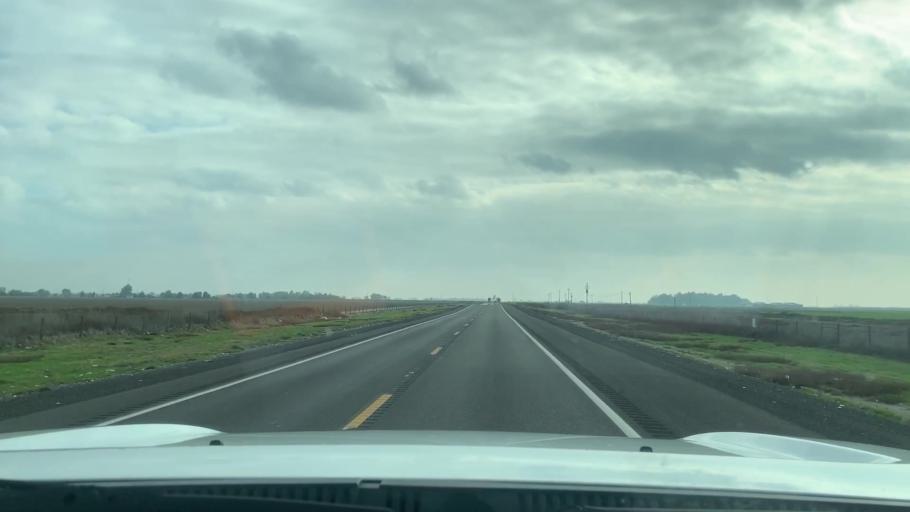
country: US
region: California
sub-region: Kings County
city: Lemoore
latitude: 36.2648
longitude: -119.8074
